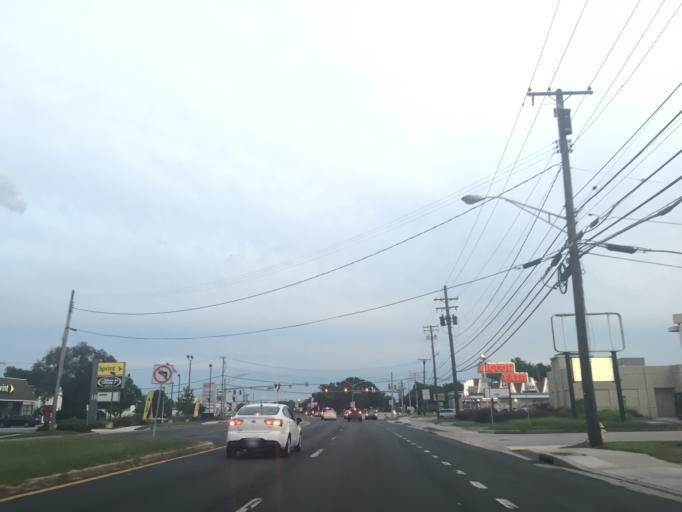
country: US
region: Maryland
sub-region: Anne Arundel County
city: Ferndale
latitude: 39.1903
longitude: -76.6138
